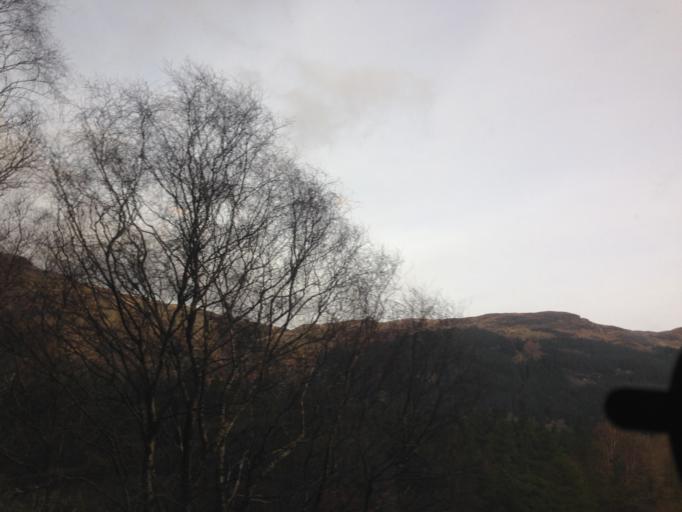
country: GB
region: Scotland
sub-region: Argyll and Bute
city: Garelochhead
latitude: 56.2144
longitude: -4.6993
